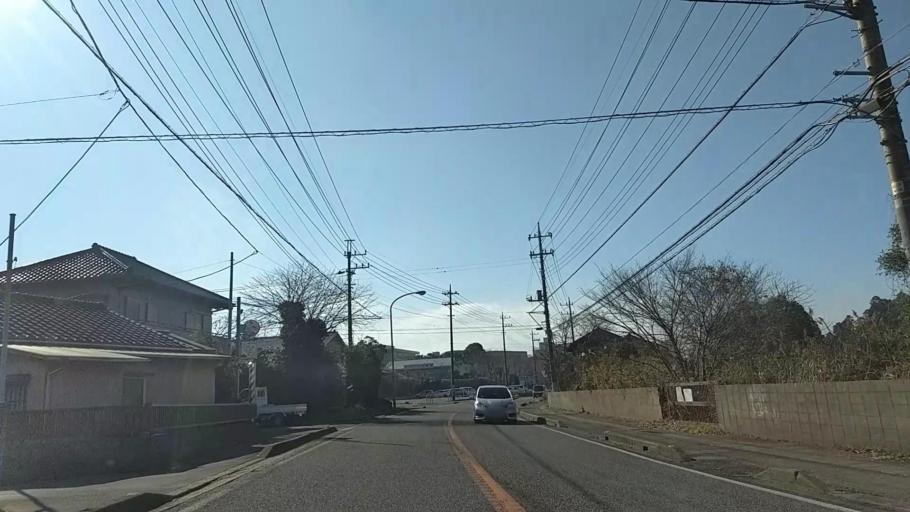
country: JP
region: Chiba
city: Yokaichiba
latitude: 35.6896
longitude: 140.5267
